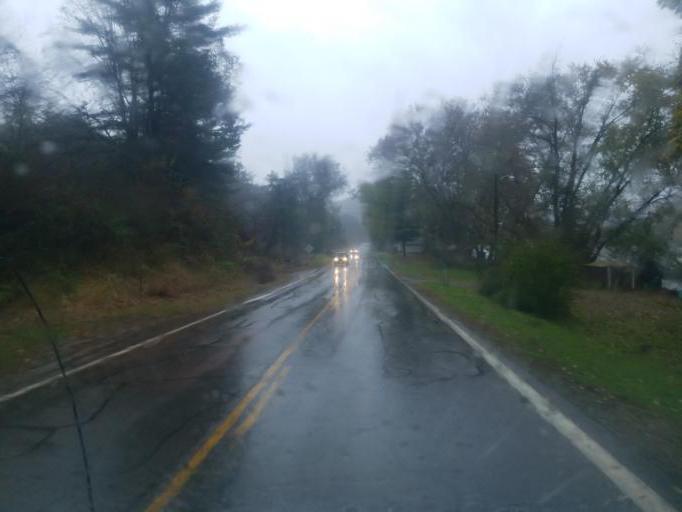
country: US
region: Ohio
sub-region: Morgan County
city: McConnelsville
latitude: 39.7738
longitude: -81.9002
